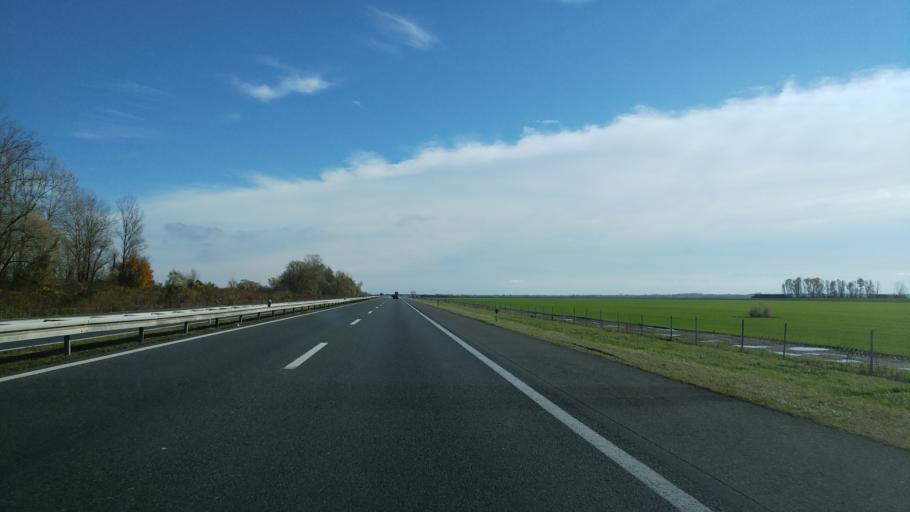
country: HR
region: Brodsko-Posavska
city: Okucani
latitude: 45.2849
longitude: 17.1077
